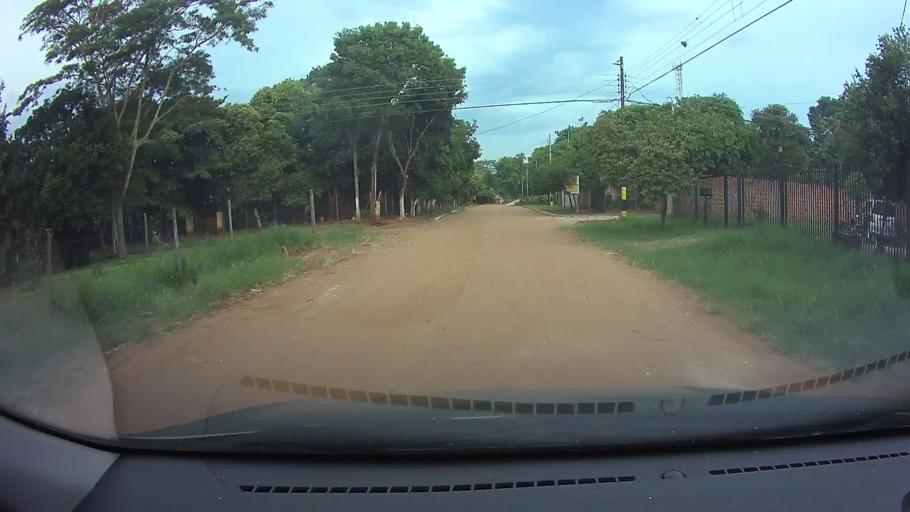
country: PY
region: Central
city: San Lorenzo
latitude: -25.2625
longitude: -57.4618
